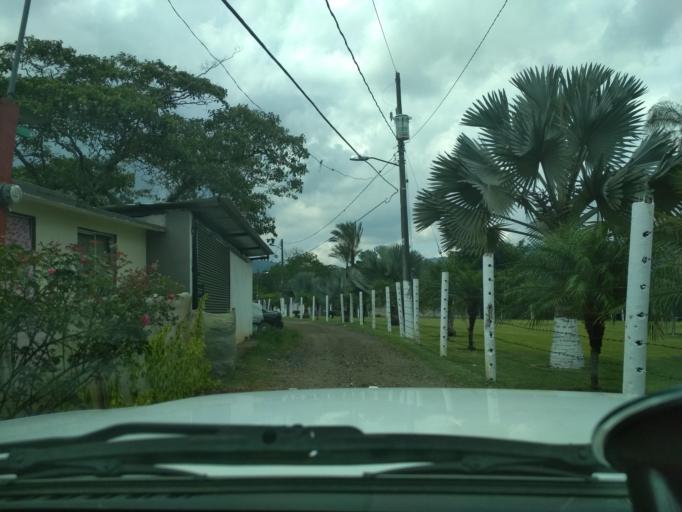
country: MX
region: Veracruz
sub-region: Cordoba
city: San Jose de Abajo [Unidad Habitacional]
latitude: 18.9204
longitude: -96.9584
